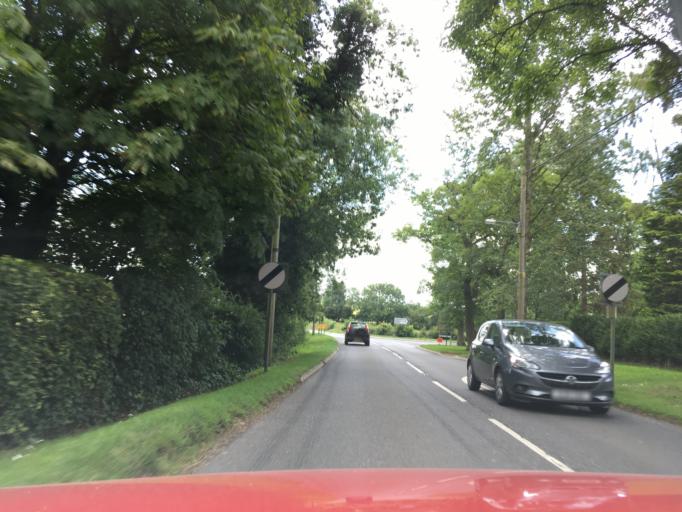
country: GB
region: England
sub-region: Buckinghamshire
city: Newton Longville
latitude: 51.9473
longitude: -0.8094
